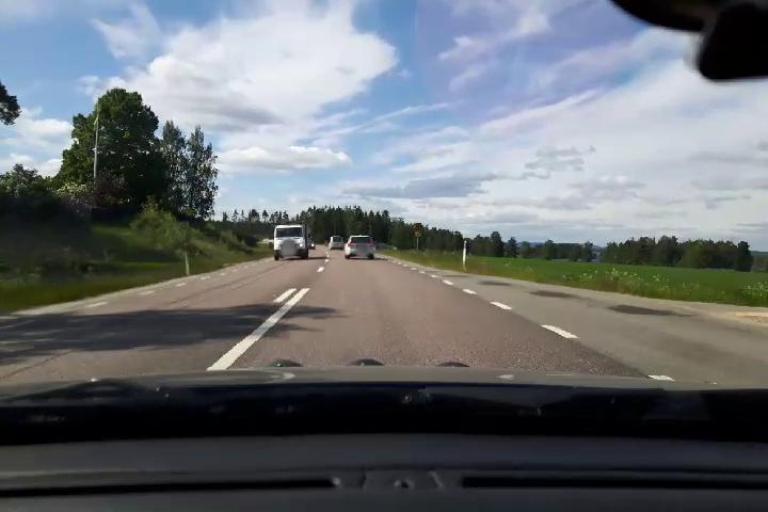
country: SE
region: Gaevleborg
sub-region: Bollnas Kommun
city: Bollnas
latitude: 61.3187
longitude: 16.4358
